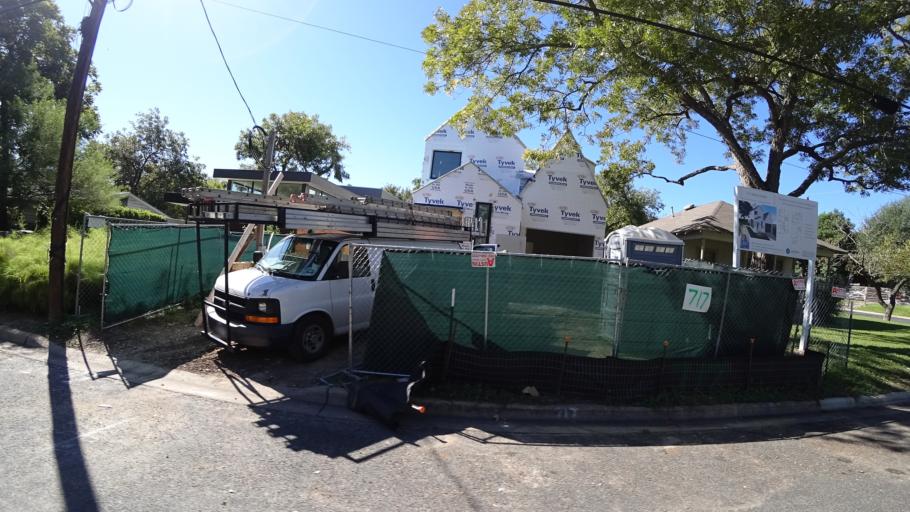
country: US
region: Texas
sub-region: Travis County
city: Austin
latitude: 30.2482
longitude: -97.7584
